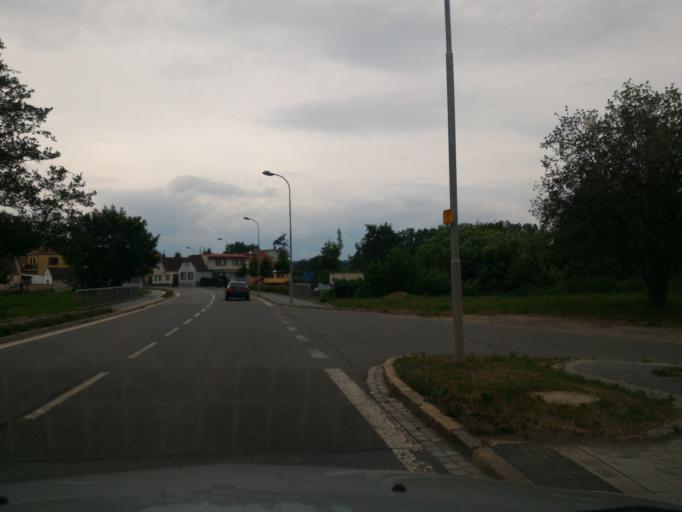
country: CZ
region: Vysocina
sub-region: Okres Jihlava
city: Telc
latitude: 49.1863
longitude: 15.4622
